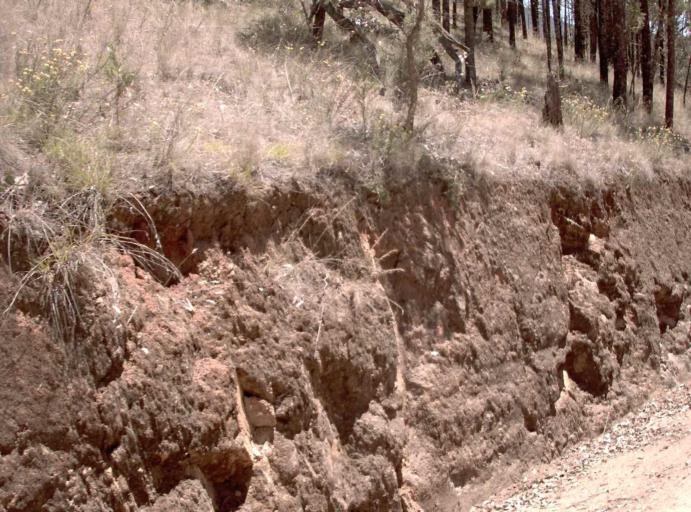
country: AU
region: New South Wales
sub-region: Snowy River
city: Jindabyne
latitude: -36.9269
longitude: 148.3756
